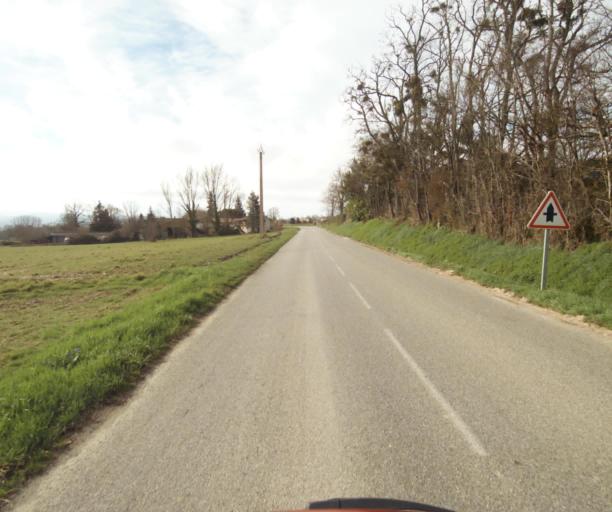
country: FR
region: Midi-Pyrenees
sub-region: Departement de l'Ariege
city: Pamiers
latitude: 43.1298
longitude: 1.5525
